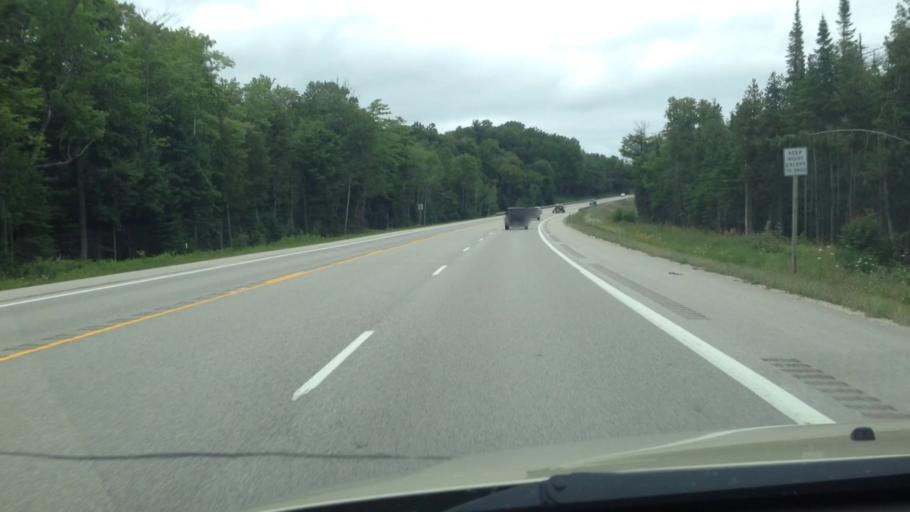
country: US
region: Michigan
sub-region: Luce County
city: Newberry
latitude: 46.0700
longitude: -85.2081
